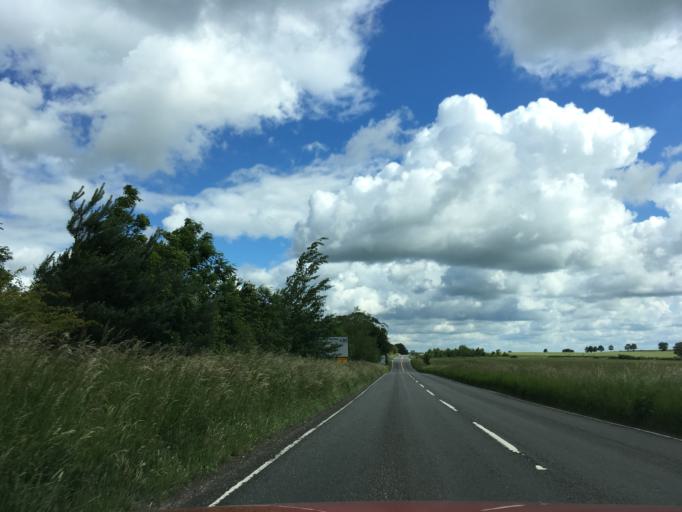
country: GB
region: England
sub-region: Oxfordshire
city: Shipton under Wychwood
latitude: 51.8356
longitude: -1.6067
